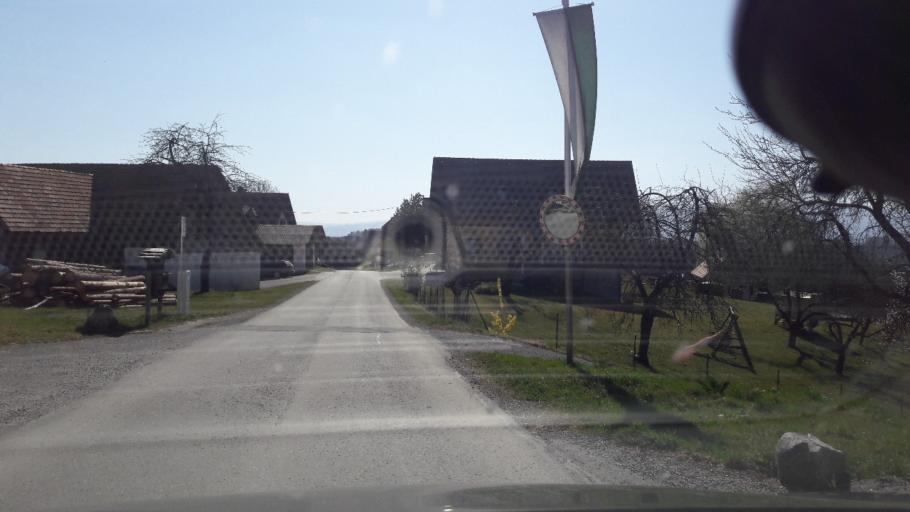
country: AT
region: Styria
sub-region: Politischer Bezirk Graz-Umgebung
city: Hitzendorf
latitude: 47.0348
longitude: 15.3152
